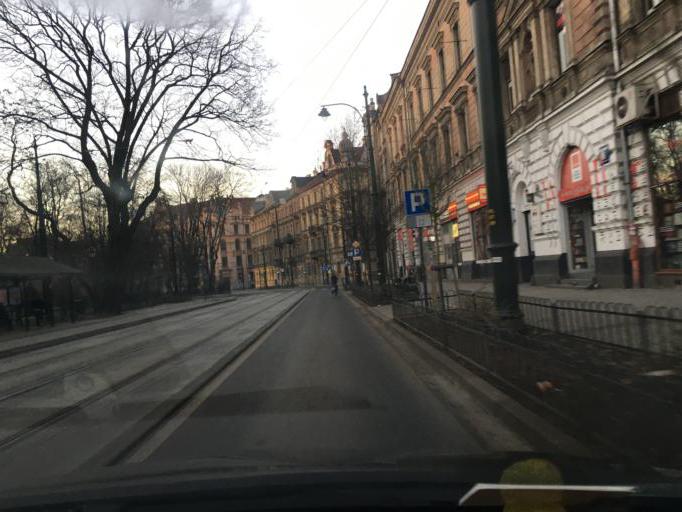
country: PL
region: Lesser Poland Voivodeship
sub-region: Krakow
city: Krakow
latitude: 50.0631
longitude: 19.9326
